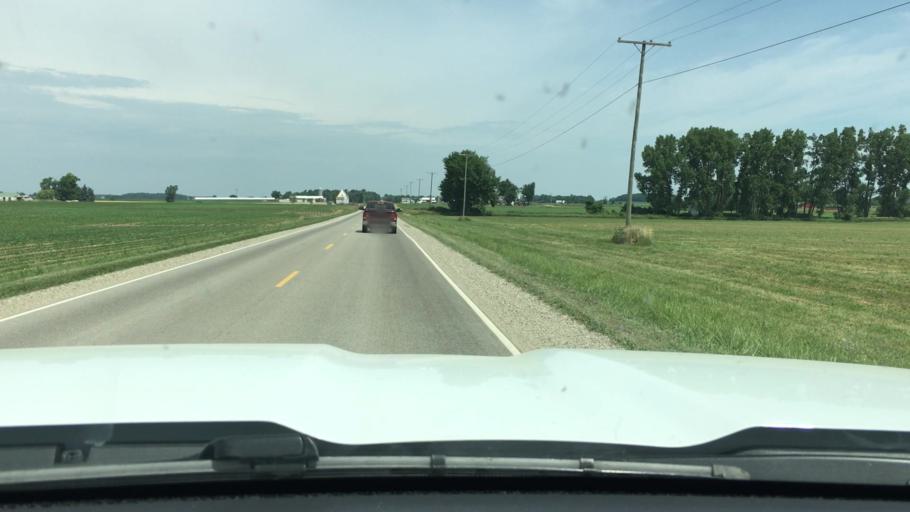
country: US
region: Michigan
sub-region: Sanilac County
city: Brown City
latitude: 43.2795
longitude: -82.9827
